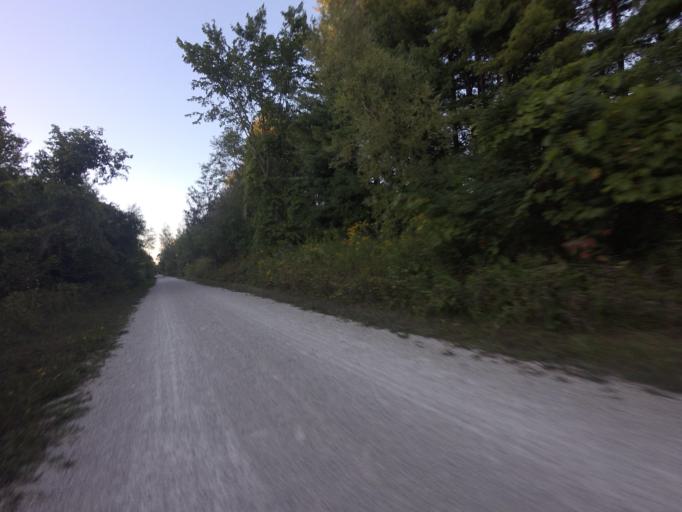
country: CA
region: Ontario
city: Brampton
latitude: 43.8983
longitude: -79.8388
